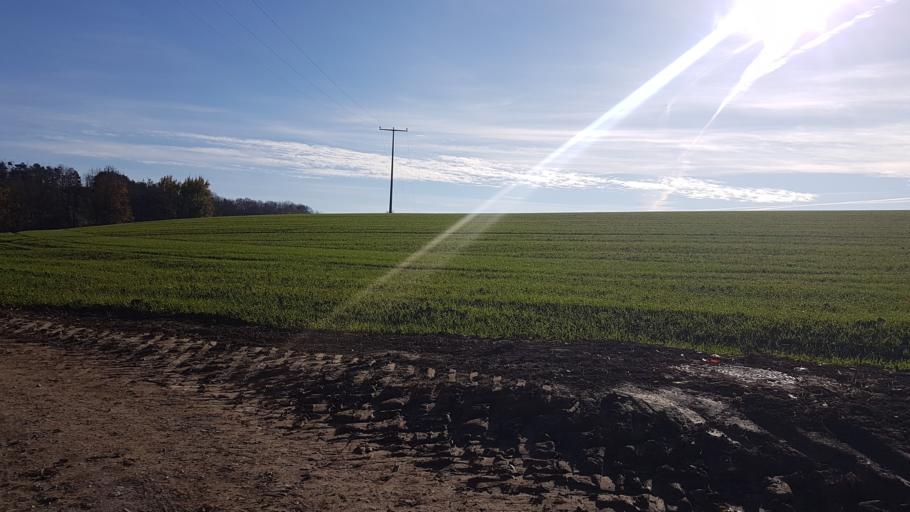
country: DE
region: Baden-Wuerttemberg
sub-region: Regierungsbezirk Stuttgart
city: Gemmingen
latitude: 49.1557
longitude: 8.9560
